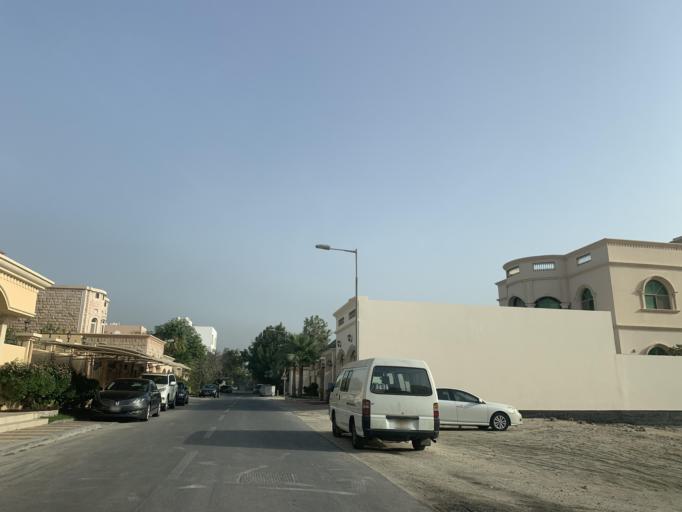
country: BH
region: Northern
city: Madinat `Isa
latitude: 26.1923
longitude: 50.5640
